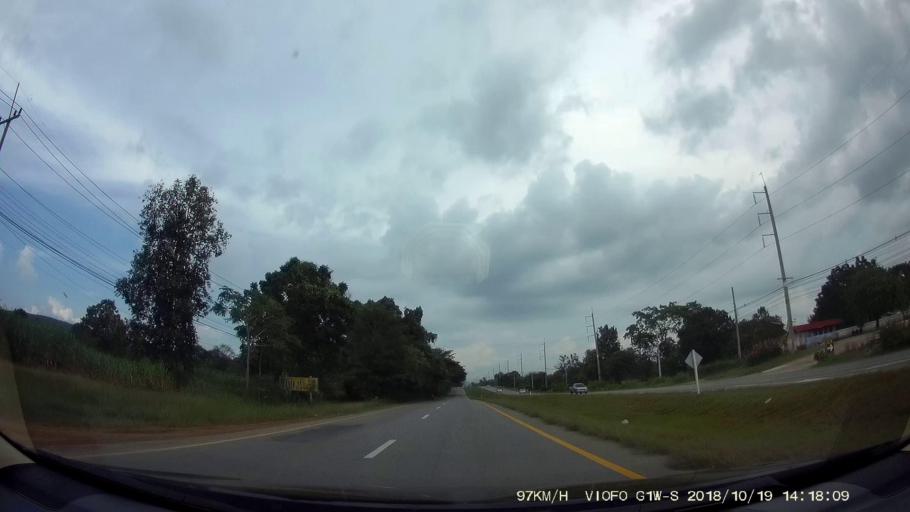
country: TH
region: Chaiyaphum
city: Khon Sawan
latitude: 16.0121
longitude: 102.2322
